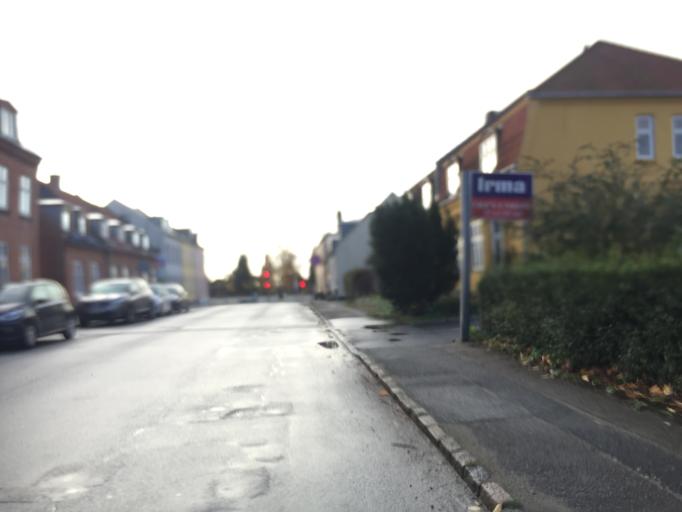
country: DK
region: Zealand
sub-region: Ringsted Kommune
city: Ringsted
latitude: 55.4435
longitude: 11.7950
